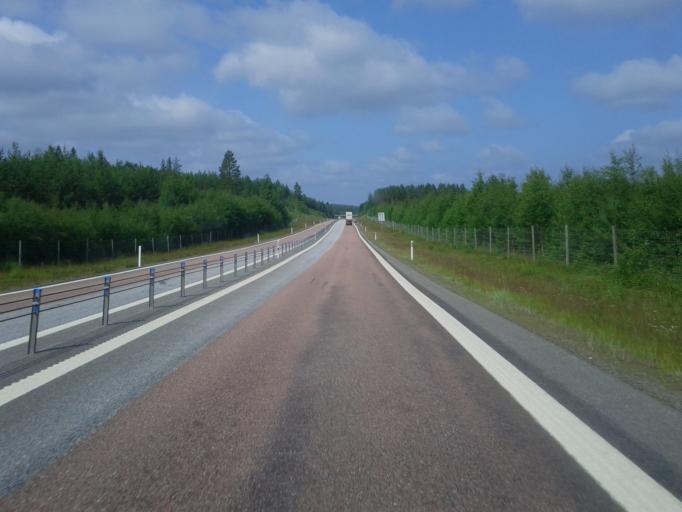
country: SE
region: Vaesterbotten
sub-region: Skelleftea Kommun
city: Soedra Bergsbyn
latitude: 64.6924
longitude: 21.0320
